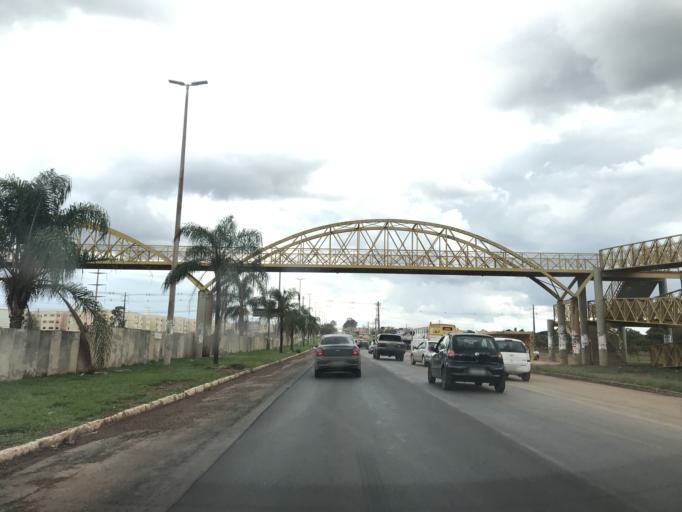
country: BR
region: Federal District
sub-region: Brasilia
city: Brasilia
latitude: -15.8919
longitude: -48.0574
